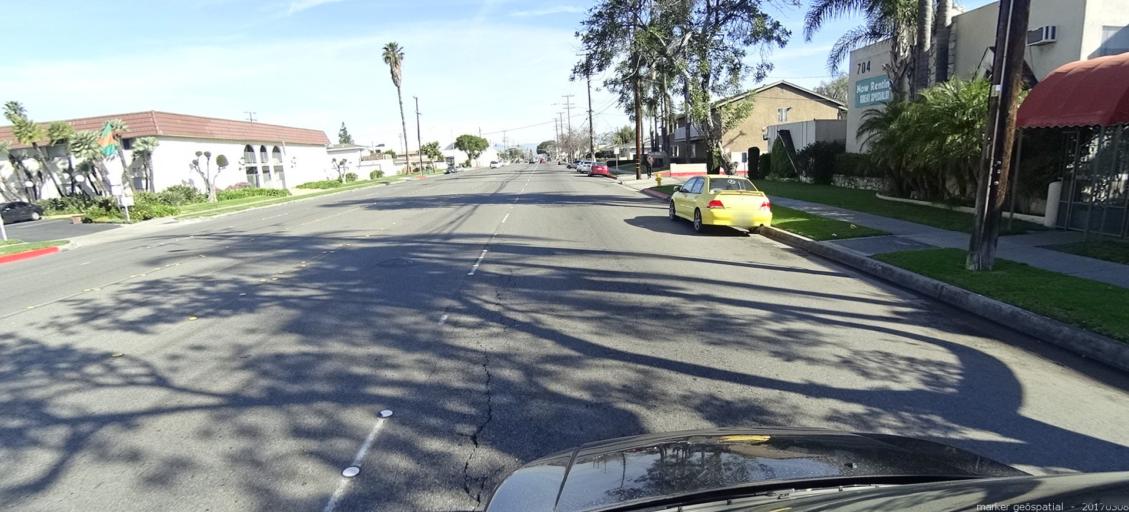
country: US
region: California
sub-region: Orange County
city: Stanton
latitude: 33.8220
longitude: -118.0108
